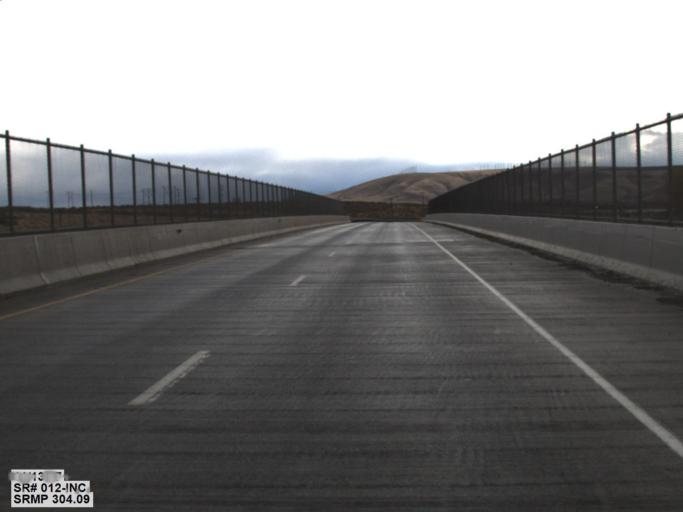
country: US
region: Washington
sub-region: Benton County
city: Finley
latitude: 46.1061
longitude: -118.9152
